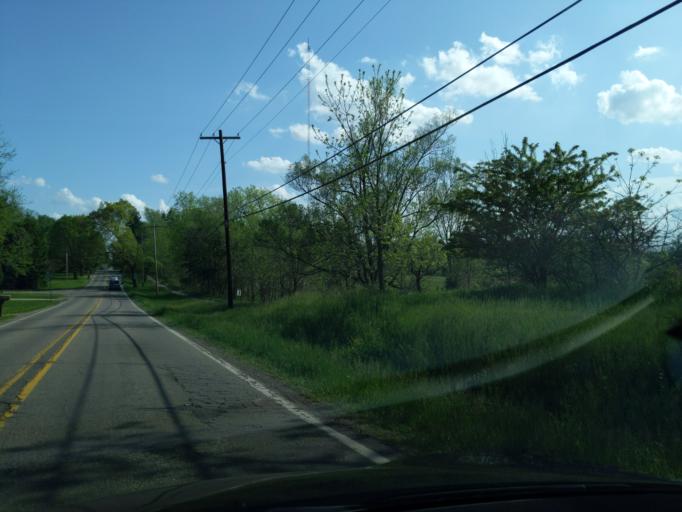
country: US
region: Michigan
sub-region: Ingham County
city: Okemos
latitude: 42.7081
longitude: -84.4104
